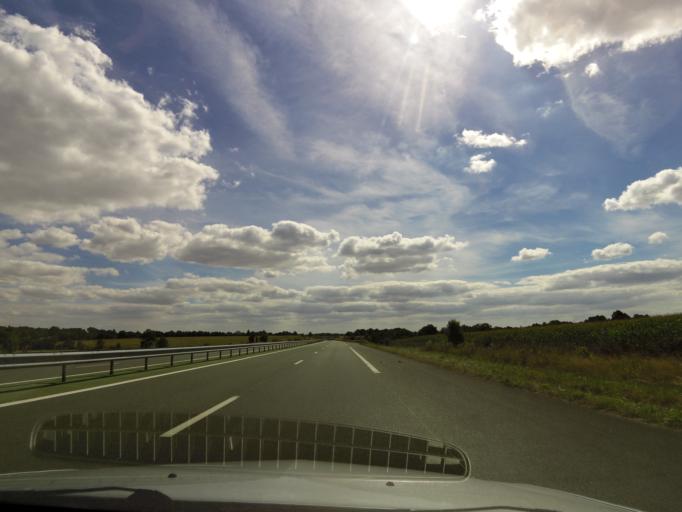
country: FR
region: Pays de la Loire
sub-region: Departement de la Vendee
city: La Ferriere
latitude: 46.7278
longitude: -1.2768
